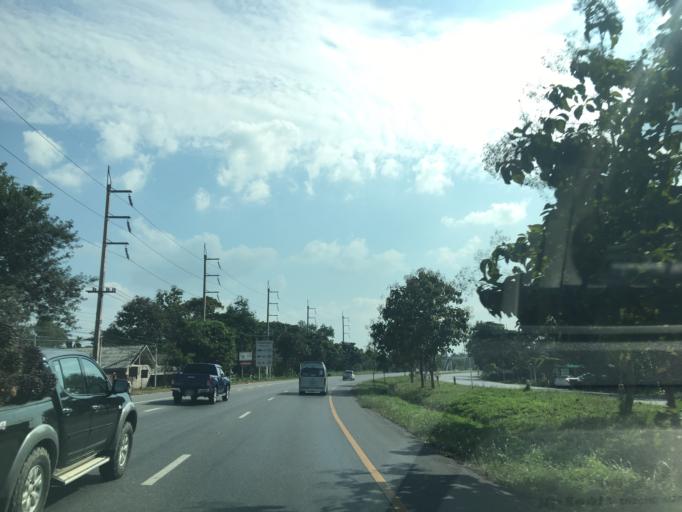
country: TH
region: Chiang Rai
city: Mae Lao
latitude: 19.7103
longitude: 99.7202
